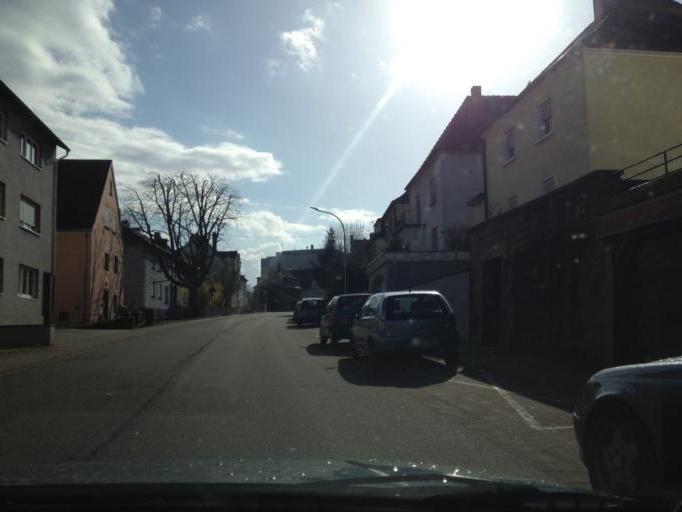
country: DE
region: Saarland
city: Neunkirchen
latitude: 49.3435
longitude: 7.1868
